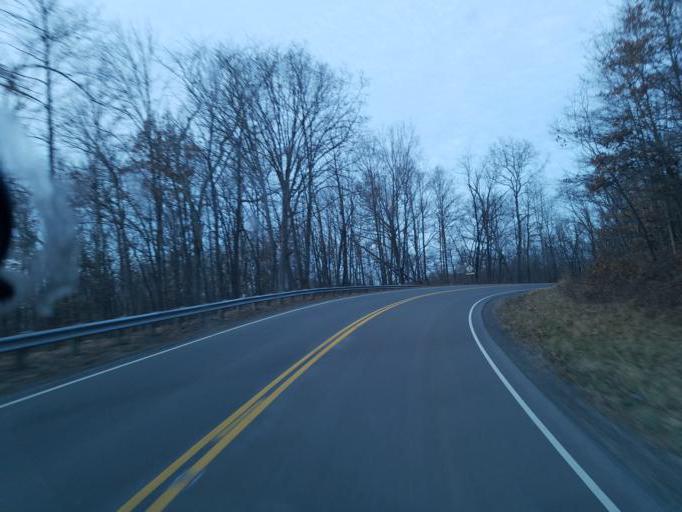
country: US
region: Ohio
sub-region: Muskingum County
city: Dresden
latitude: 40.1711
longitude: -82.0290
